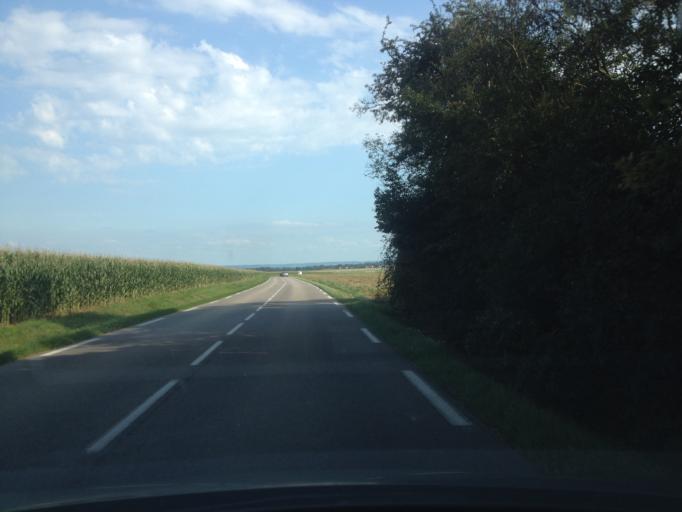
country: FR
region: Lower Normandy
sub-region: Departement du Calvados
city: Moult
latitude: 49.0770
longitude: -0.1397
